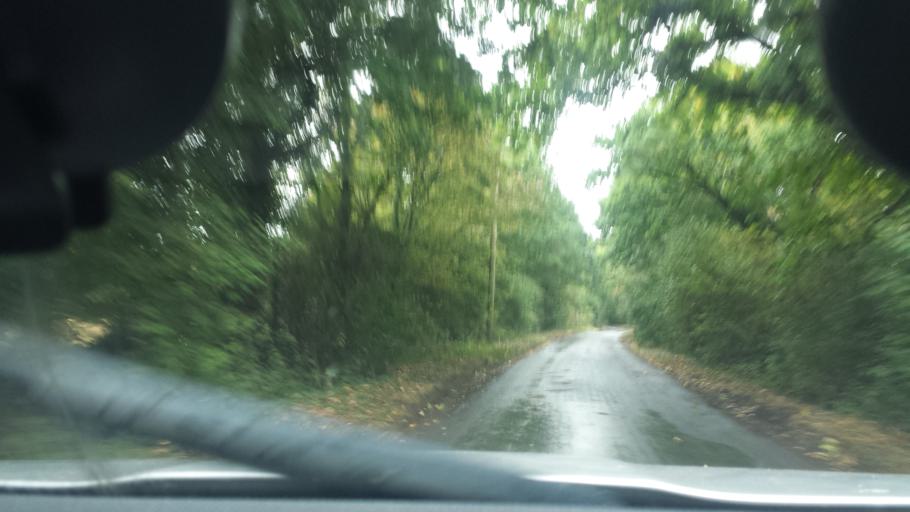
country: GB
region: England
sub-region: Kent
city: Staplehurst
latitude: 51.1751
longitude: 0.5412
